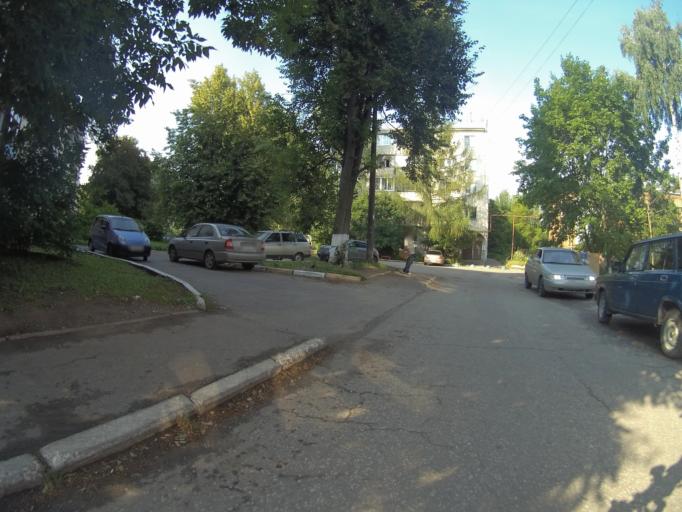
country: RU
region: Vladimir
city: Bogolyubovo
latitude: 56.1709
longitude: 40.4876
